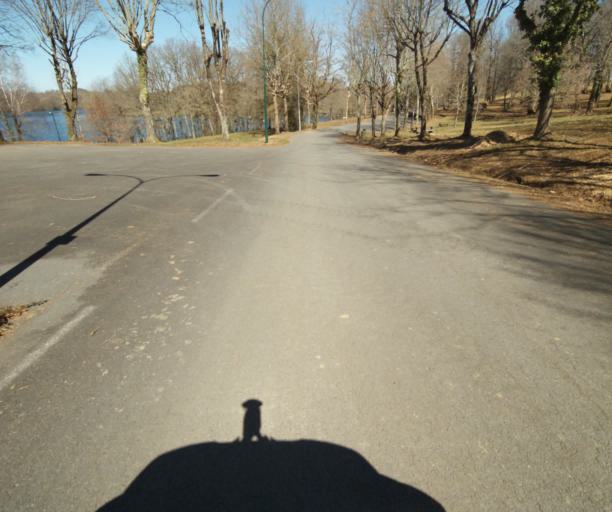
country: FR
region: Limousin
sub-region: Departement de la Correze
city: Seilhac
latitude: 45.3775
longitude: 1.6997
